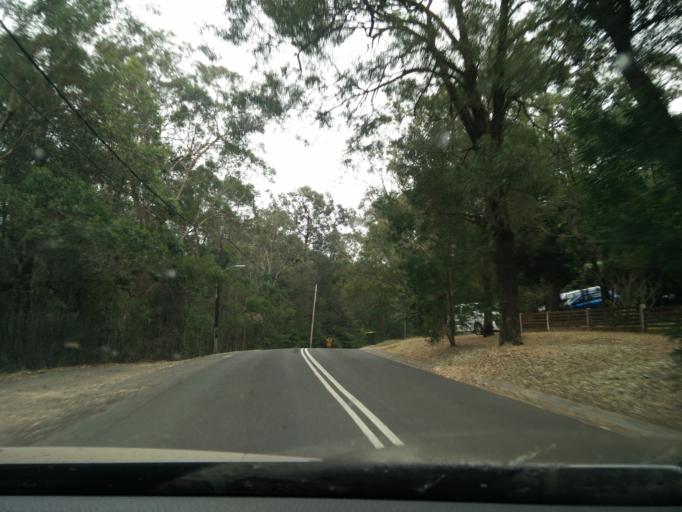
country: AU
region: New South Wales
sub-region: Blue Mountains Municipality
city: Glenbrook
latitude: -33.7717
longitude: 150.6236
